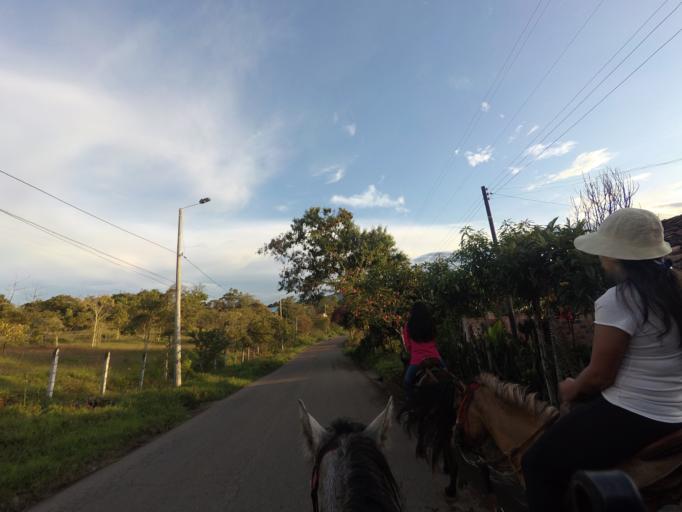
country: CO
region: Huila
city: San Agustin
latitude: 1.8909
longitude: -76.2717
